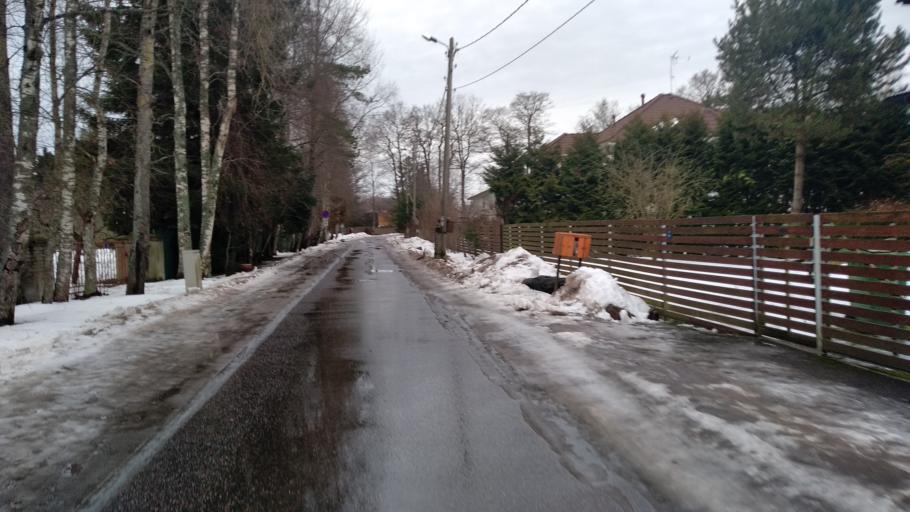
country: EE
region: Harju
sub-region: Harku vald
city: Tabasalu
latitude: 59.4475
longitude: 24.6050
